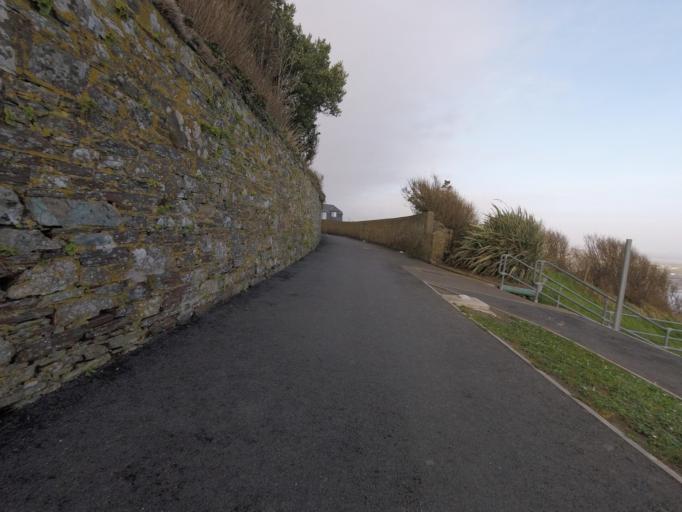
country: IE
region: Munster
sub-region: Waterford
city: Tra Mhor
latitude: 52.1574
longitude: -7.1541
